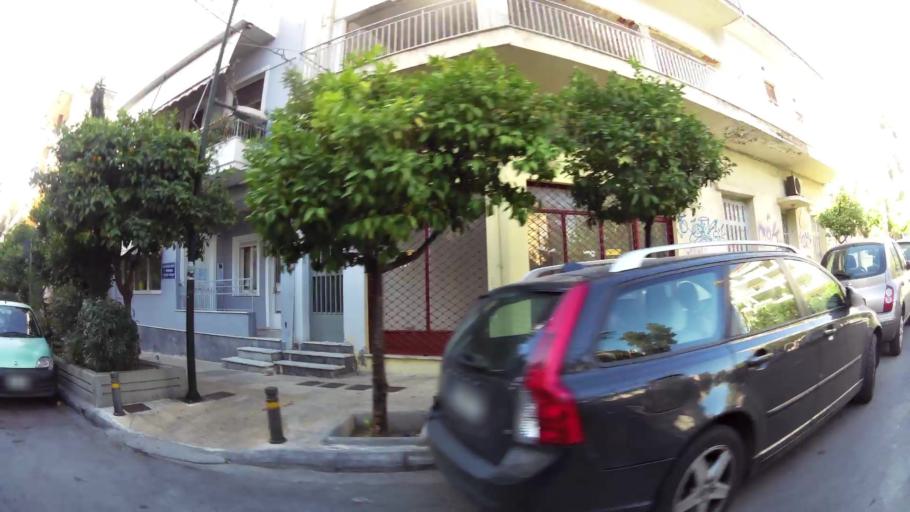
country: GR
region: Attica
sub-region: Nomos Piraios
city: Korydallos
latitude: 37.9800
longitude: 23.6501
